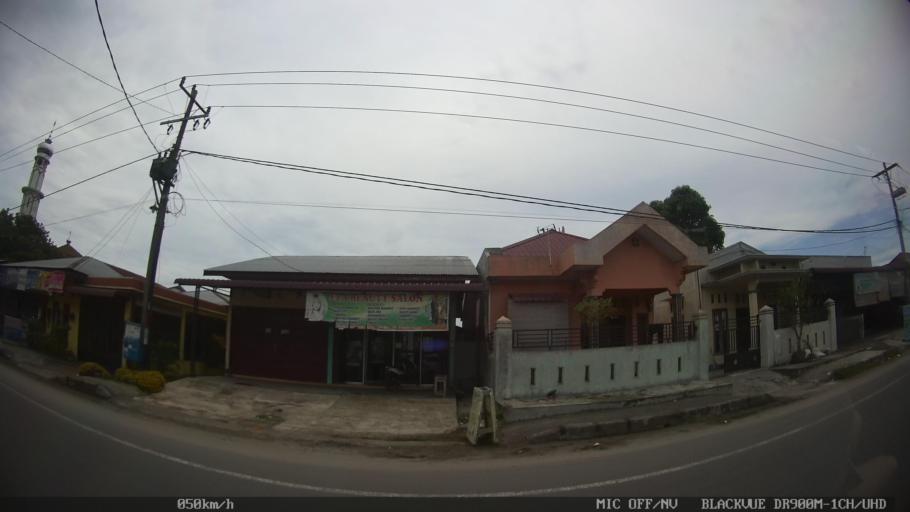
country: ID
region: North Sumatra
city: Sunggal
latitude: 3.6078
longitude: 98.5759
